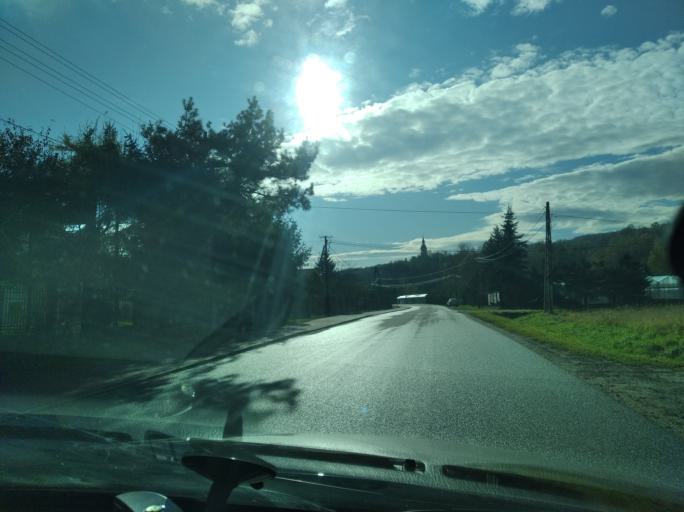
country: PL
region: Subcarpathian Voivodeship
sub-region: Powiat debicki
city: Brzeznica
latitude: 50.0536
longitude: 21.4842
